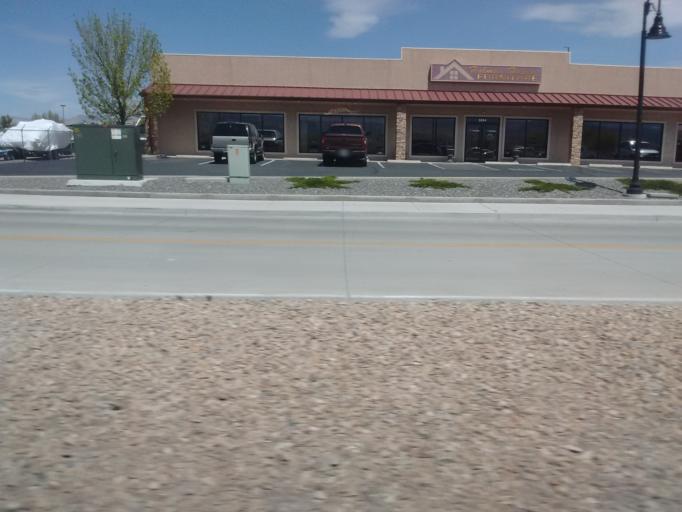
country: US
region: Colorado
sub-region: Mesa County
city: Redlands
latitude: 39.0838
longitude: -108.5910
